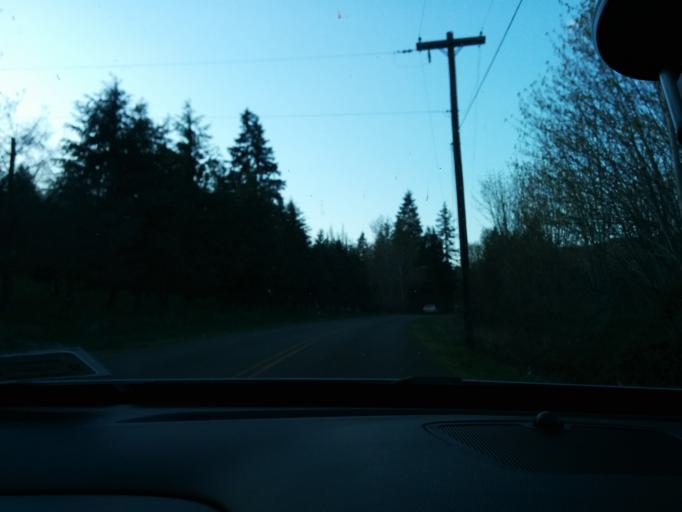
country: US
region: Washington
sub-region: Snohomish County
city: Gold Bar
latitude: 47.8835
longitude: -121.7347
